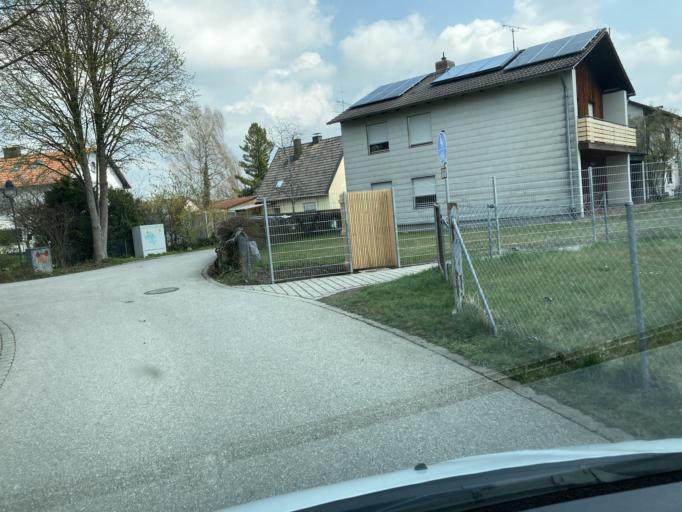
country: DE
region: Bavaria
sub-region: Upper Bavaria
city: Grafing bei Munchen
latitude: 48.0400
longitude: 11.9648
